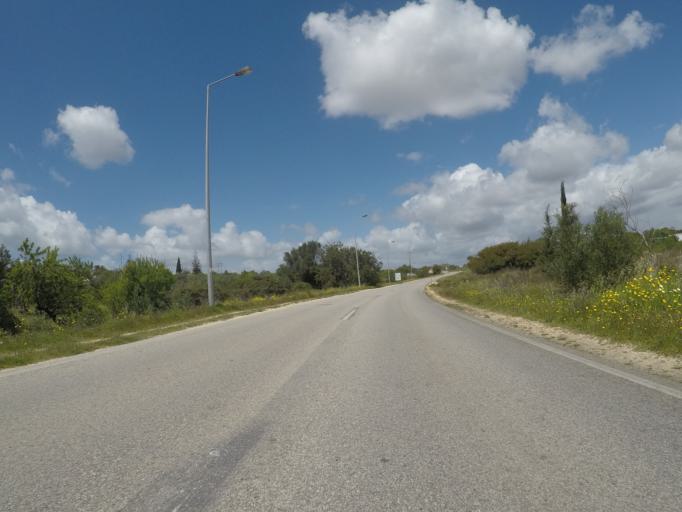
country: PT
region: Faro
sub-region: Silves
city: Armacao de Pera
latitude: 37.1170
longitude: -8.3487
